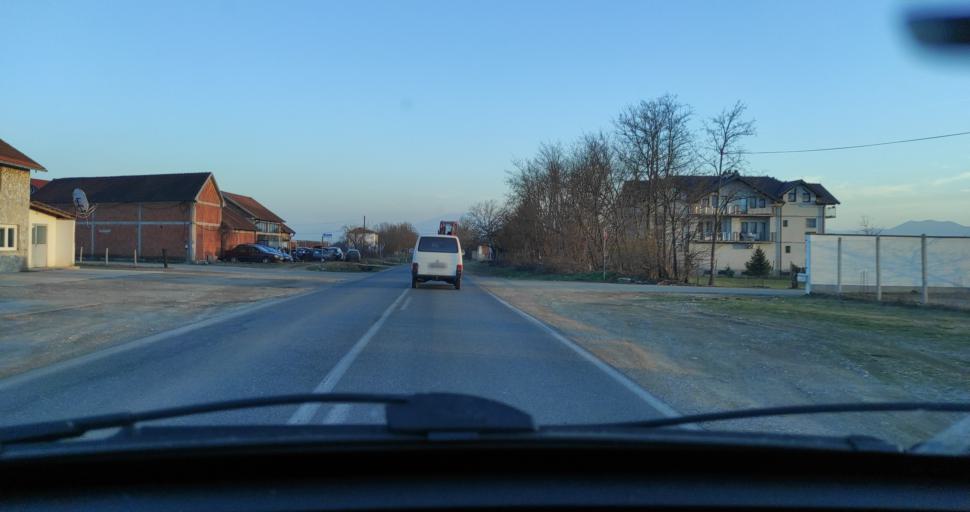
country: XK
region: Gjakova
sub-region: Komuna e Decanit
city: Gllogjan
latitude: 42.4433
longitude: 20.3657
